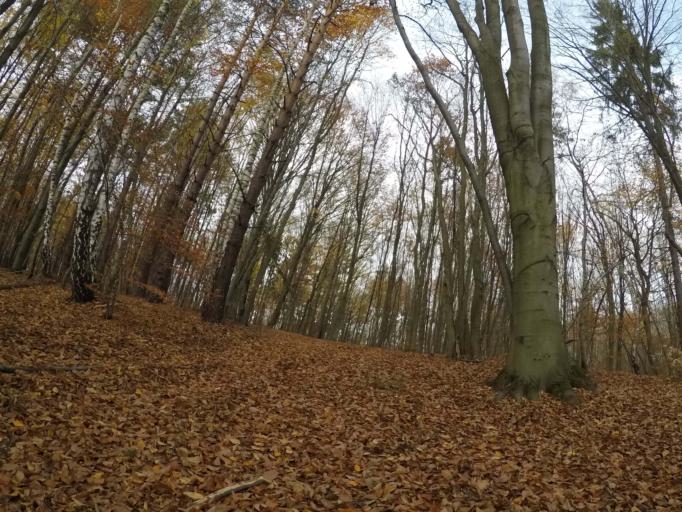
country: SK
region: Presovsky
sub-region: Okres Presov
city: Presov
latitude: 48.9520
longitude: 21.2042
